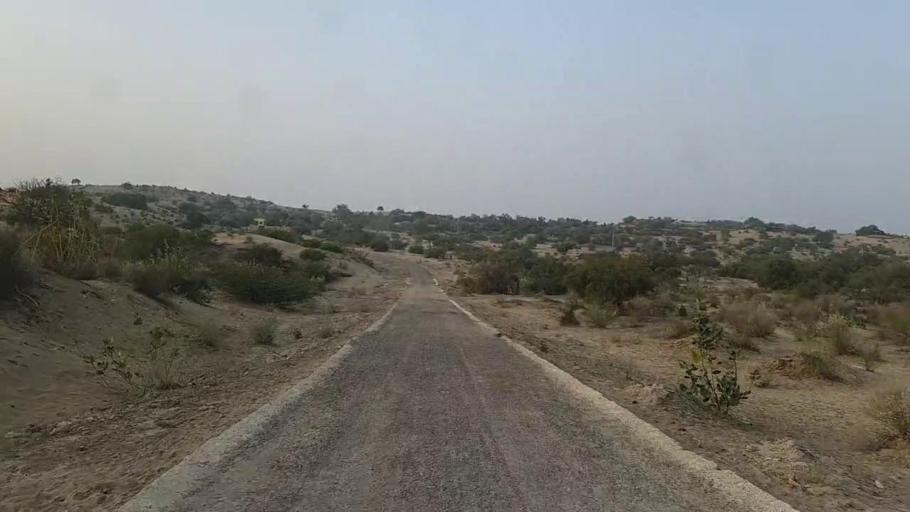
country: PK
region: Sindh
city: Naukot
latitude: 24.6793
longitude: 69.4589
